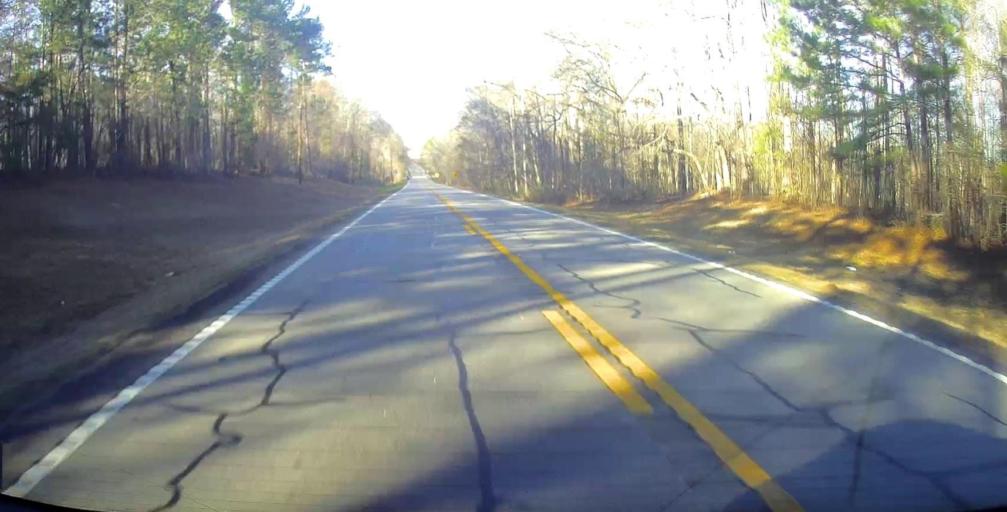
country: US
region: Georgia
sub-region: Meriwether County
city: Manchester
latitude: 32.8696
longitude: -84.5983
